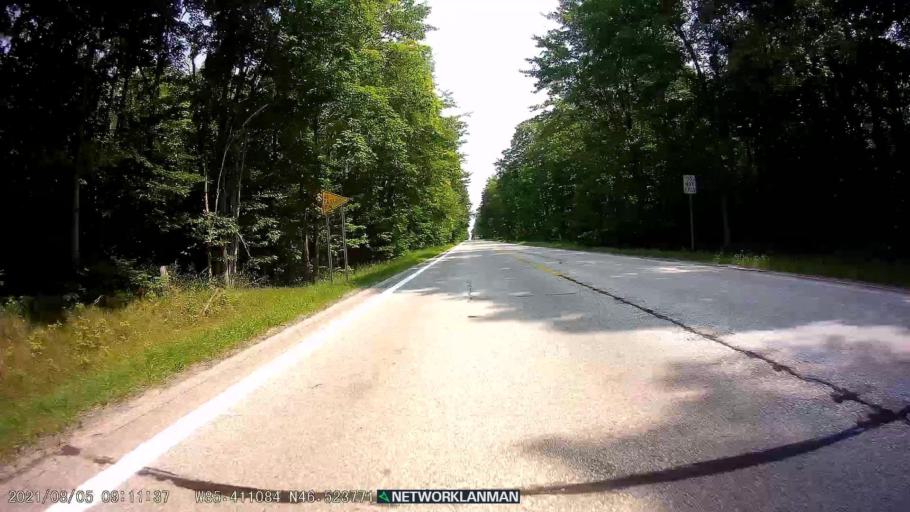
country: US
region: Michigan
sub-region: Luce County
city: Newberry
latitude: 46.5236
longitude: -85.4113
